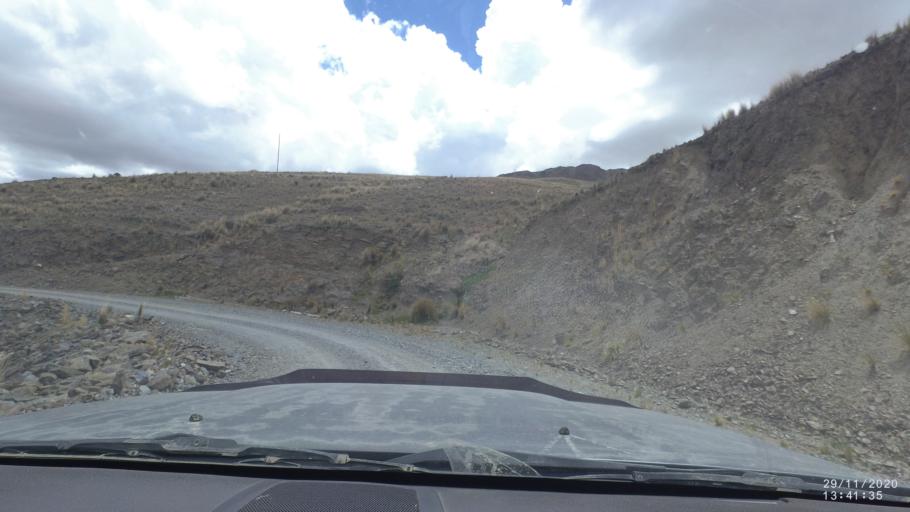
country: BO
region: Cochabamba
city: Cochabamba
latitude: -17.1324
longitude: -66.3241
